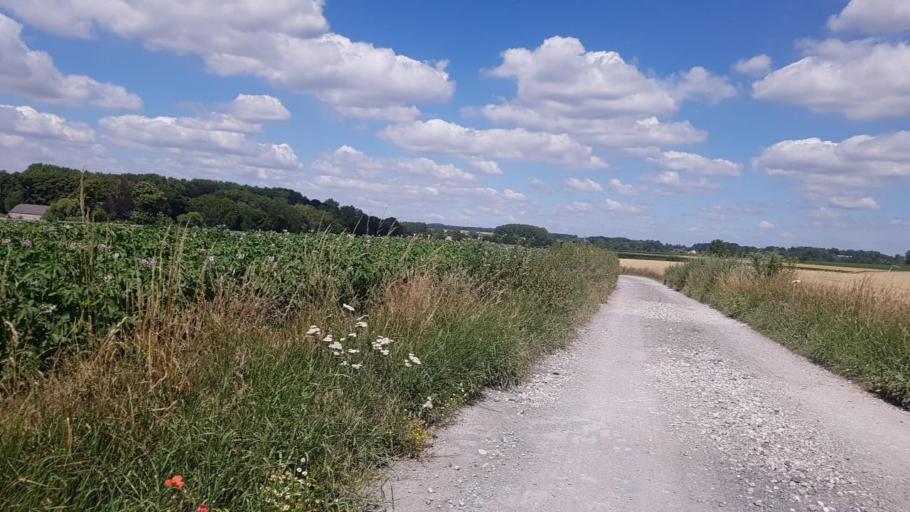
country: BE
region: Wallonia
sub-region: Province du Hainaut
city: Thuin
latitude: 50.3134
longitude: 4.3498
